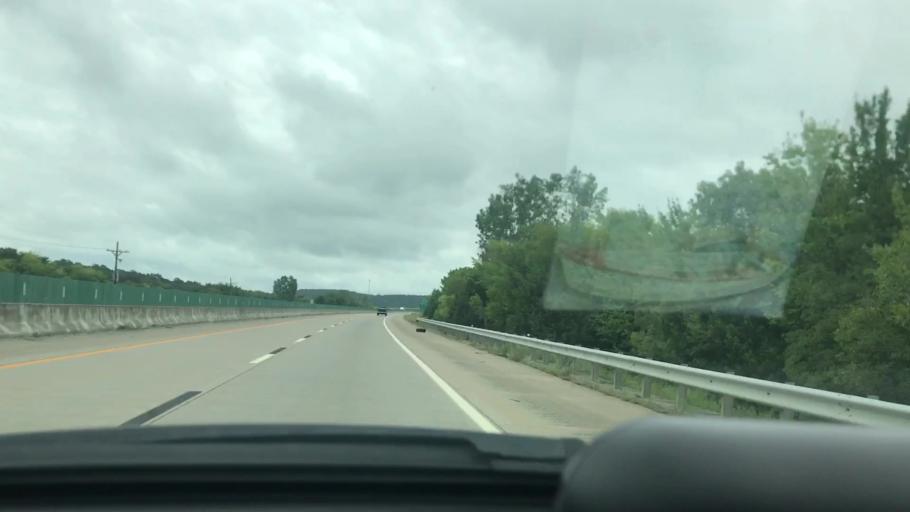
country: US
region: Oklahoma
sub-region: Pittsburg County
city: Krebs
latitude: 35.0932
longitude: -95.6997
